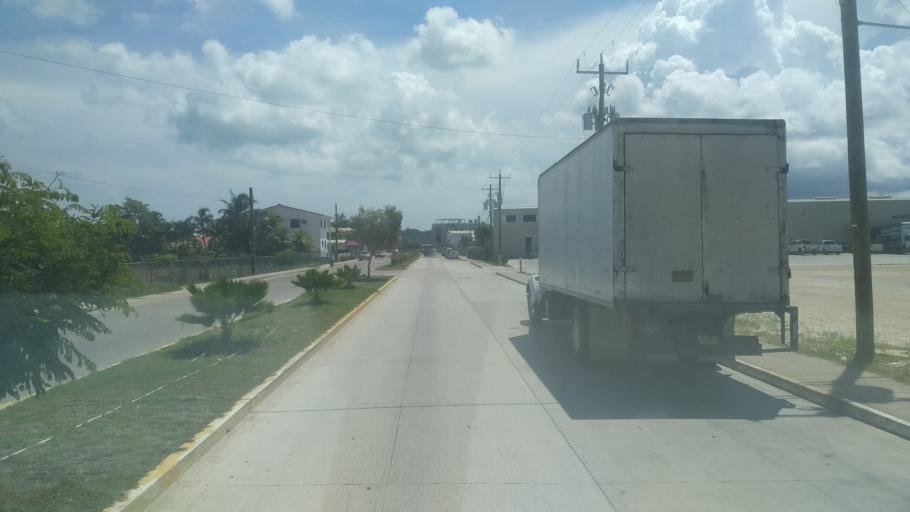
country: BZ
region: Belize
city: Belize City
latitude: 17.5125
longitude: -88.2212
